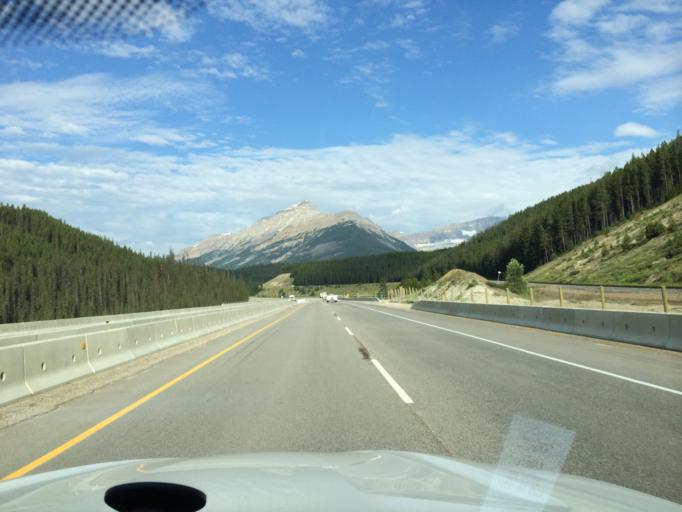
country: CA
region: Alberta
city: Lake Louise
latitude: 51.4428
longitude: -116.2291
